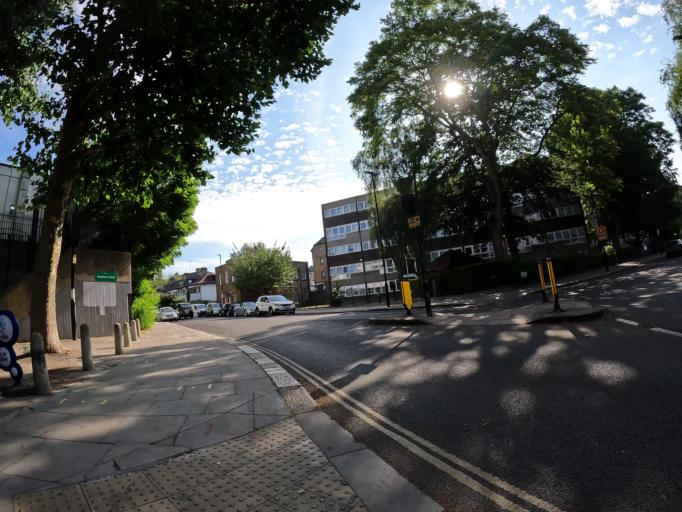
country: GB
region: England
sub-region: Greater London
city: Belsize Park
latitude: 51.5584
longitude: -0.1650
